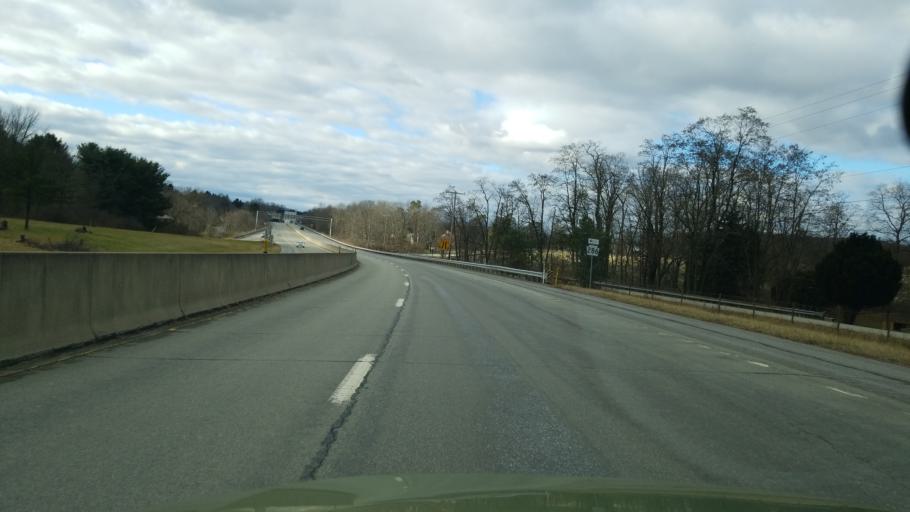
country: US
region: Pennsylvania
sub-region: Indiana County
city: Chevy Chase Heights
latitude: 40.6261
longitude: -79.1318
